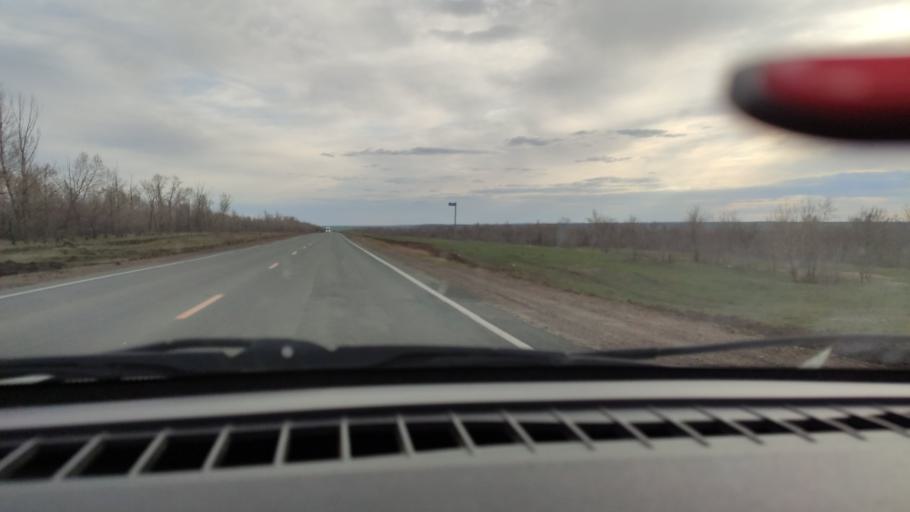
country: RU
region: Orenburg
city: Sakmara
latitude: 52.2370
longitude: 55.3445
